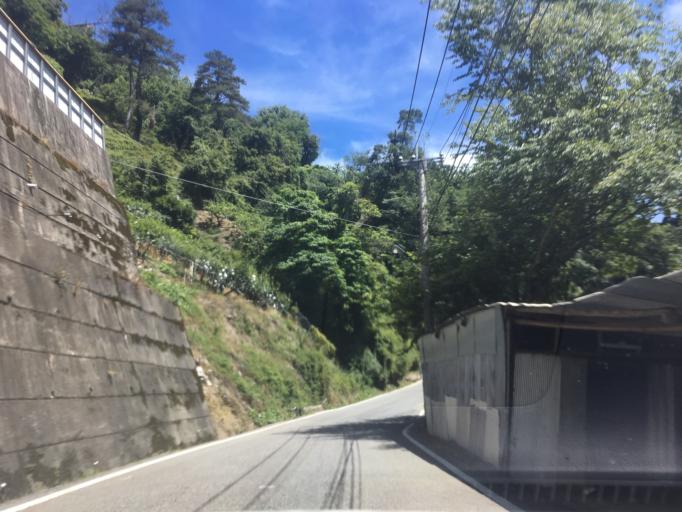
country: TW
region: Taiwan
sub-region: Nantou
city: Puli
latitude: 24.2426
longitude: 121.2546
